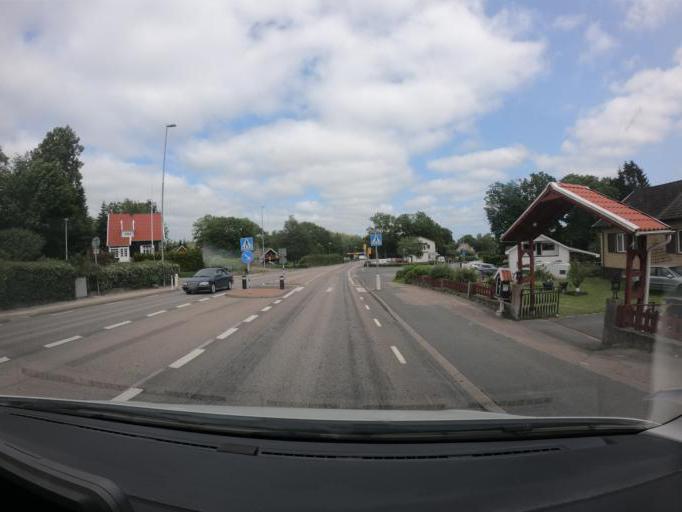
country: SE
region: Skane
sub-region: Hassleholms Kommun
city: Sosdala
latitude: 56.1635
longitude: 13.5860
